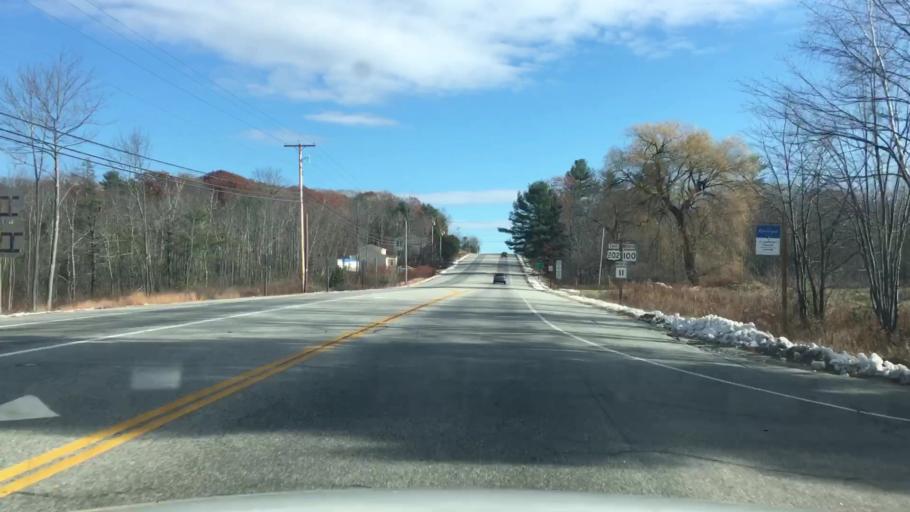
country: US
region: Maine
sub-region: Kennebec County
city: Winthrop
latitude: 44.3198
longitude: -69.9252
